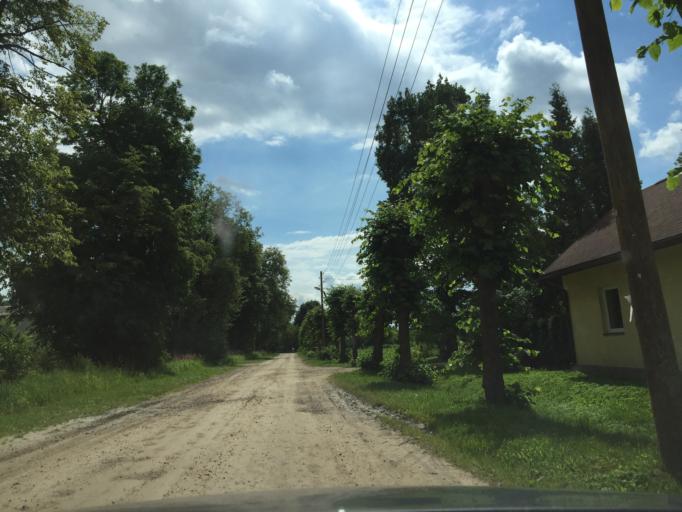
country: LV
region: Jelgava
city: Jelgava
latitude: 56.6484
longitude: 23.6800
